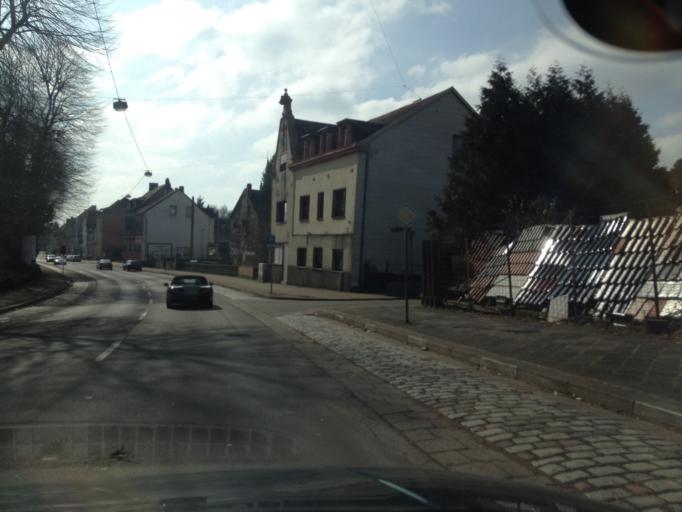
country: DE
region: Saarland
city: Friedrichsthal
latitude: 49.3128
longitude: 7.0836
